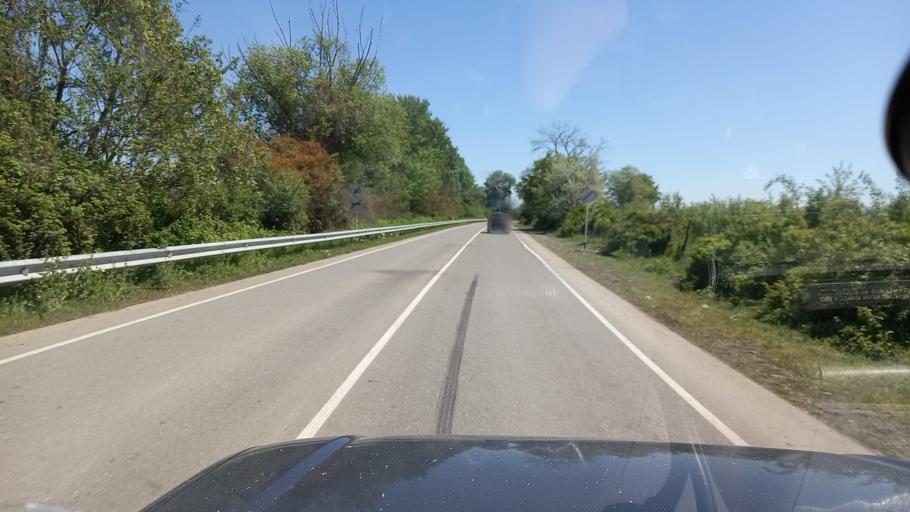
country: RU
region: Dagestan
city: Samur
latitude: 41.7361
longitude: 48.4710
